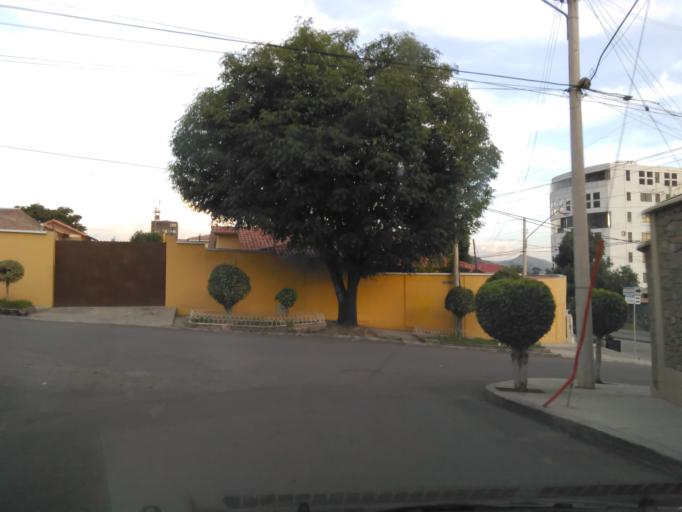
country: BO
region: Cochabamba
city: Cochabamba
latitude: -17.3653
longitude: -66.1589
